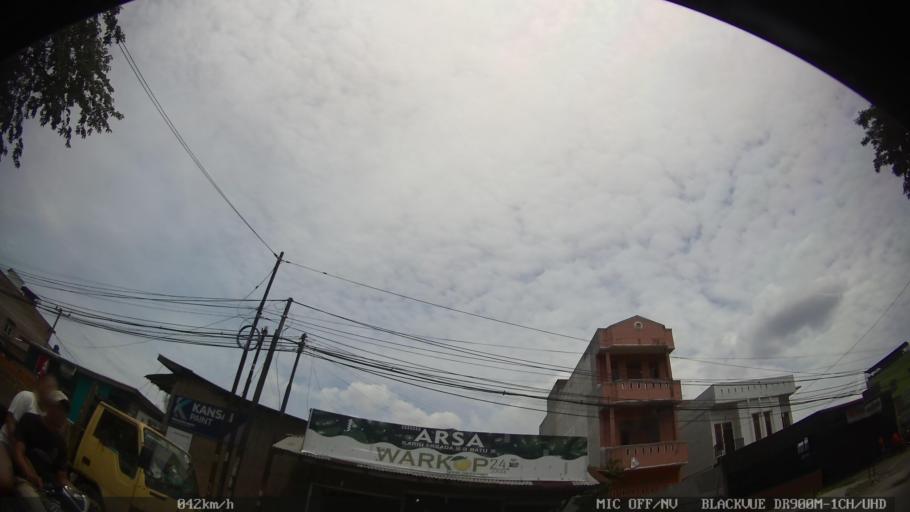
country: ID
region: North Sumatra
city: Deli Tua
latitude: 3.5334
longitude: 98.6474
